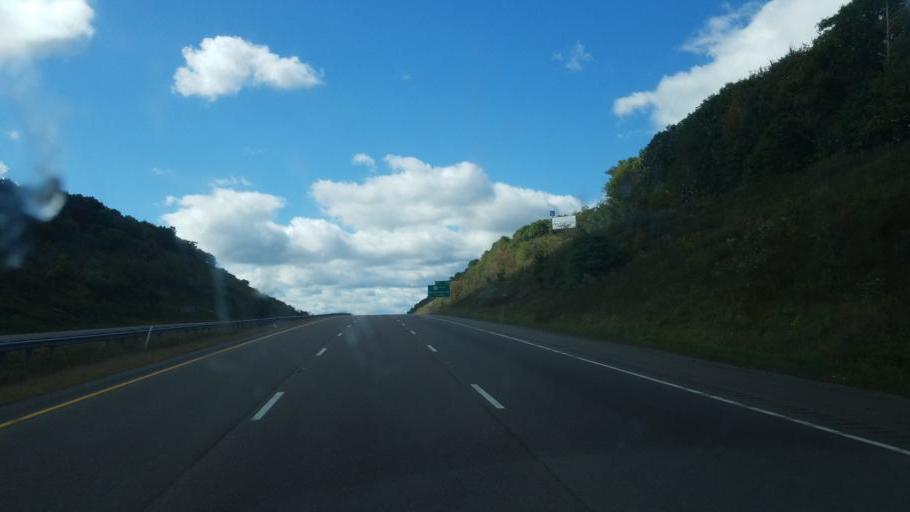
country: US
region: Pennsylvania
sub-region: Somerset County
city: Meyersdale
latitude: 39.6847
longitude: -79.0843
